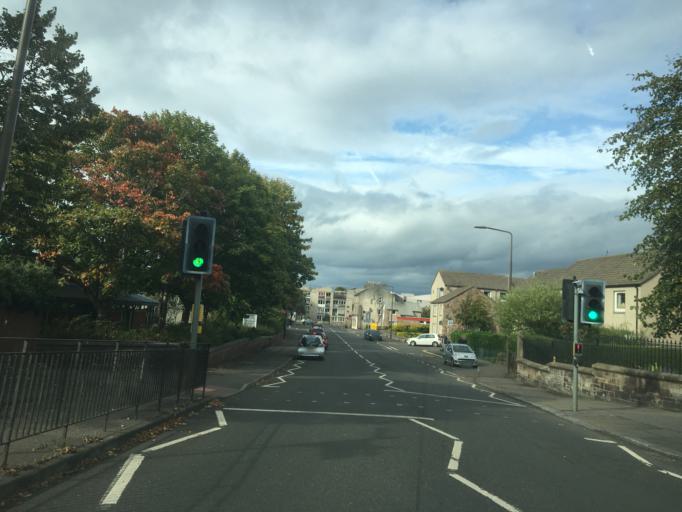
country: GB
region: Scotland
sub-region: East Lothian
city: Musselburgh
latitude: 55.9385
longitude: -3.0477
